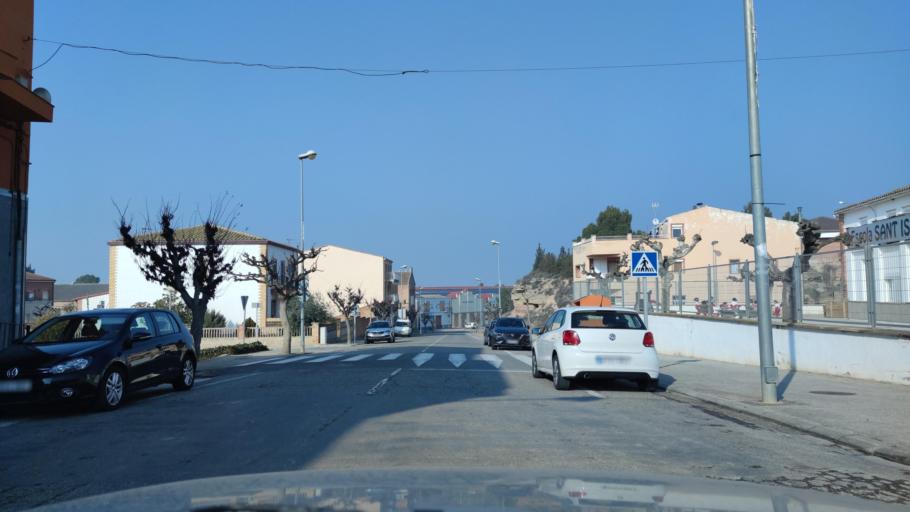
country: ES
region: Catalonia
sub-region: Provincia de Lleida
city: Sunyer
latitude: 41.5606
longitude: 0.5888
